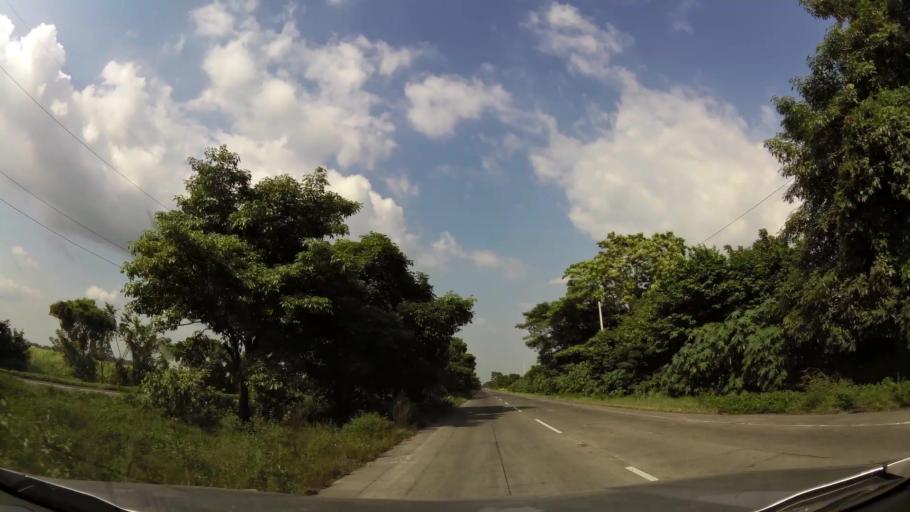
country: GT
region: Escuintla
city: Puerto San Jose
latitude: 14.0267
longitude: -90.7817
